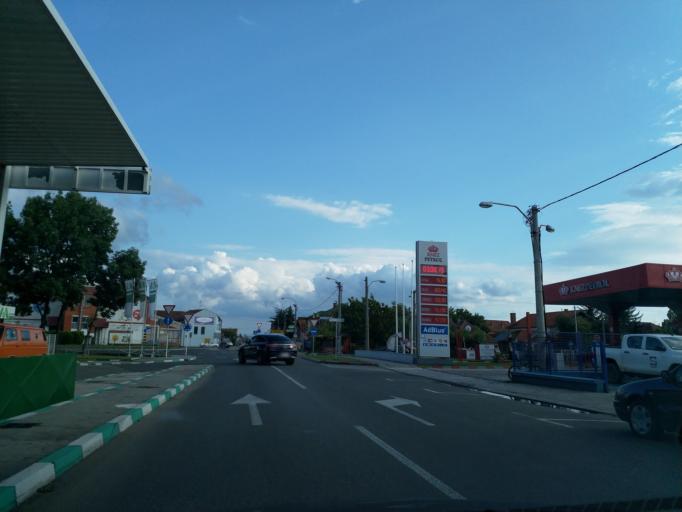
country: RS
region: Central Serbia
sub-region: Pomoravski Okrug
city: Paracin
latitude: 43.8538
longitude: 21.4129
